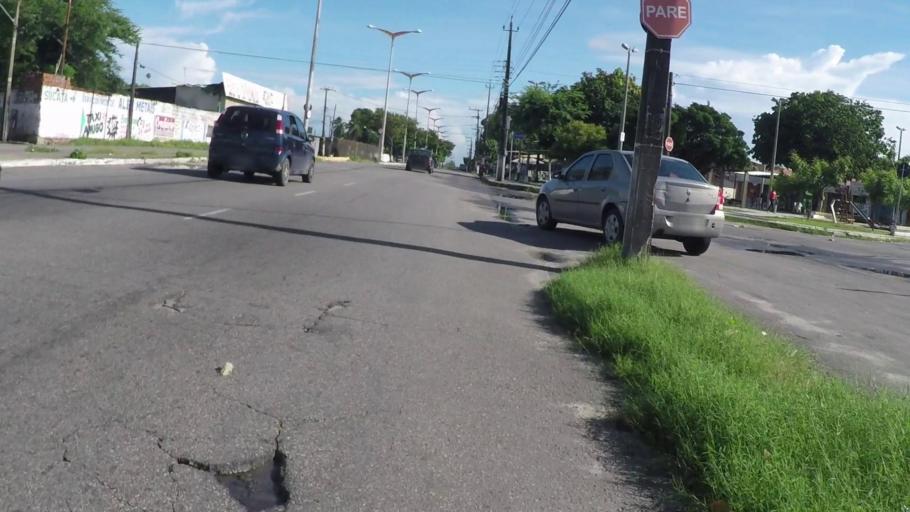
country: BR
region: Ceara
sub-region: Fortaleza
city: Fortaleza
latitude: -3.7092
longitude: -38.5900
